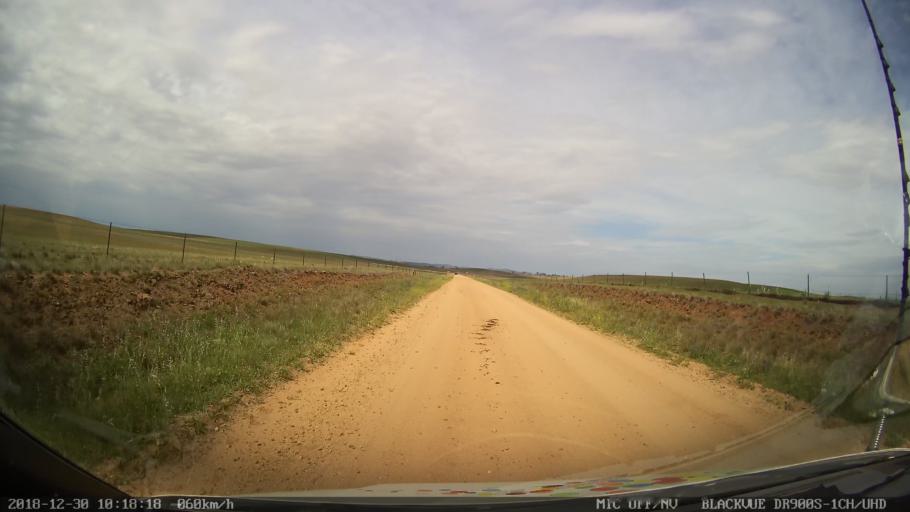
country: AU
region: New South Wales
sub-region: Snowy River
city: Berridale
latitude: -36.5514
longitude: 149.0106
